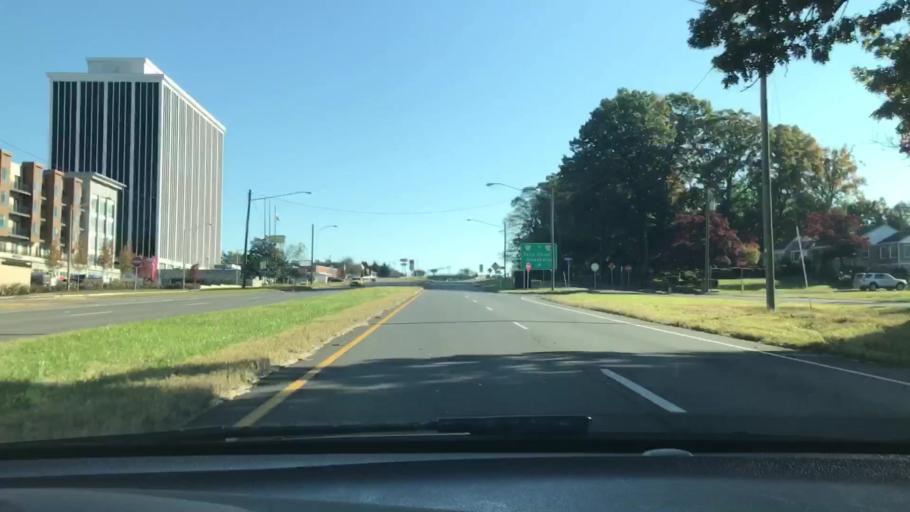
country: US
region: Virginia
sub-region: Fairfax County
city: Seven Corners
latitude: 38.8717
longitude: -77.1623
